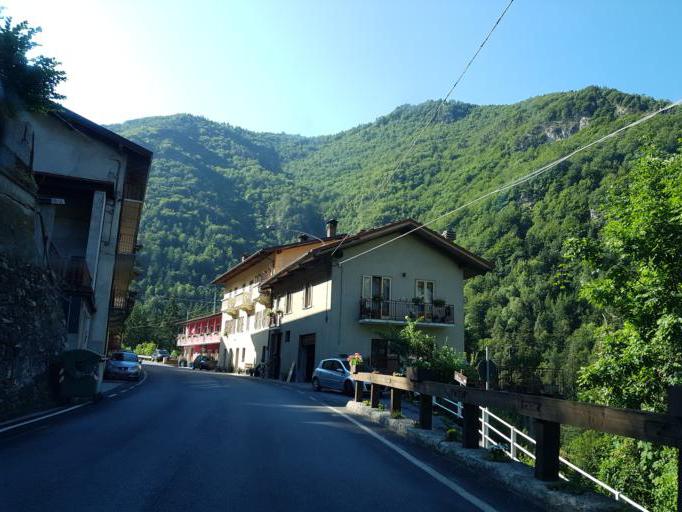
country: IT
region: Piedmont
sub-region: Provincia di Cuneo
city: Macra
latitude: 44.4991
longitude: 7.1792
